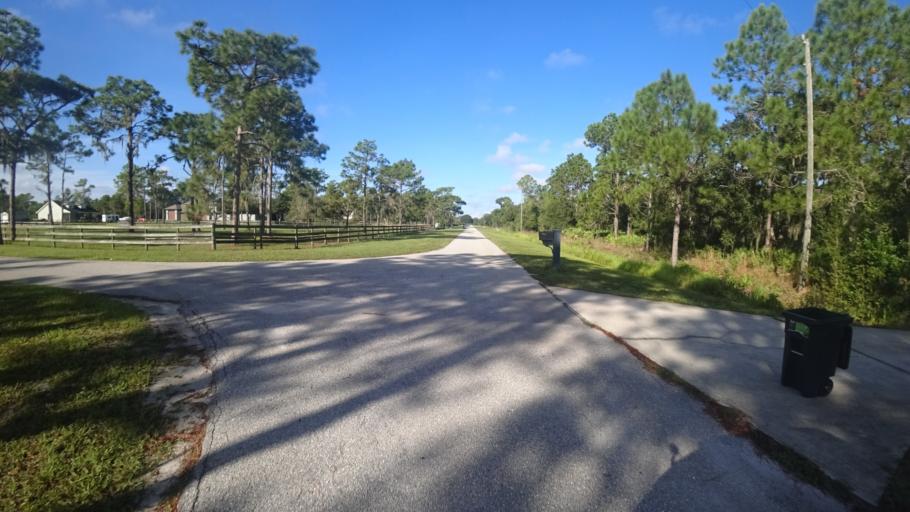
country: US
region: Florida
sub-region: Sarasota County
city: The Meadows
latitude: 27.4166
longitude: -82.3223
